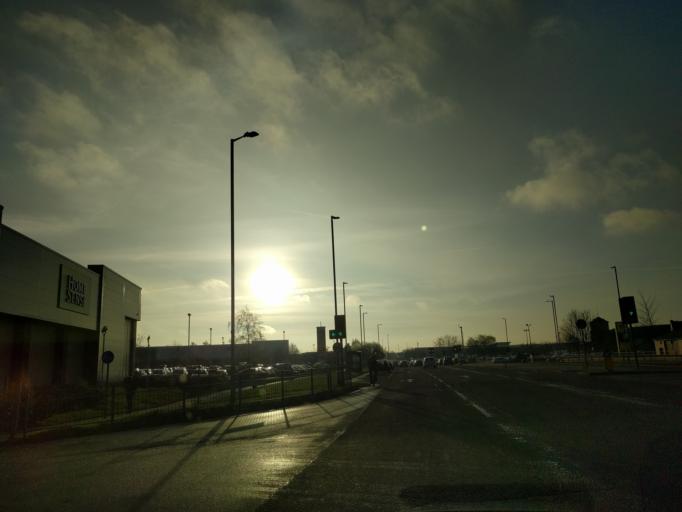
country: GB
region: England
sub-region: Lincolnshire
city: Lincoln
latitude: 53.2251
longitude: -0.5516
